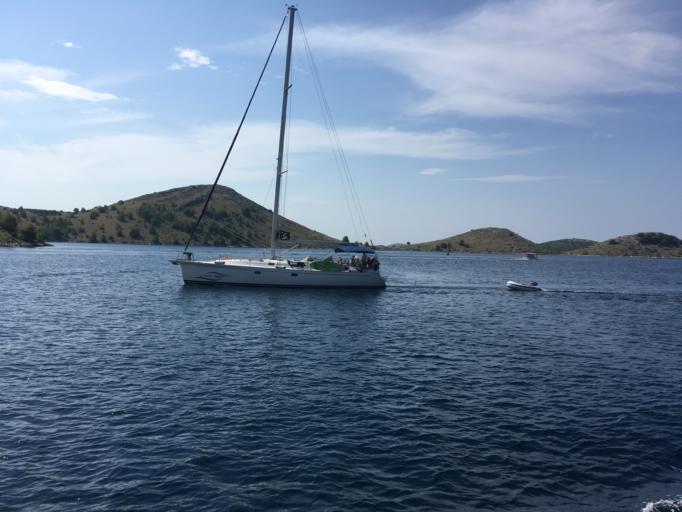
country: HR
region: Zadarska
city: Sali
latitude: 43.8876
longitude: 15.2117
